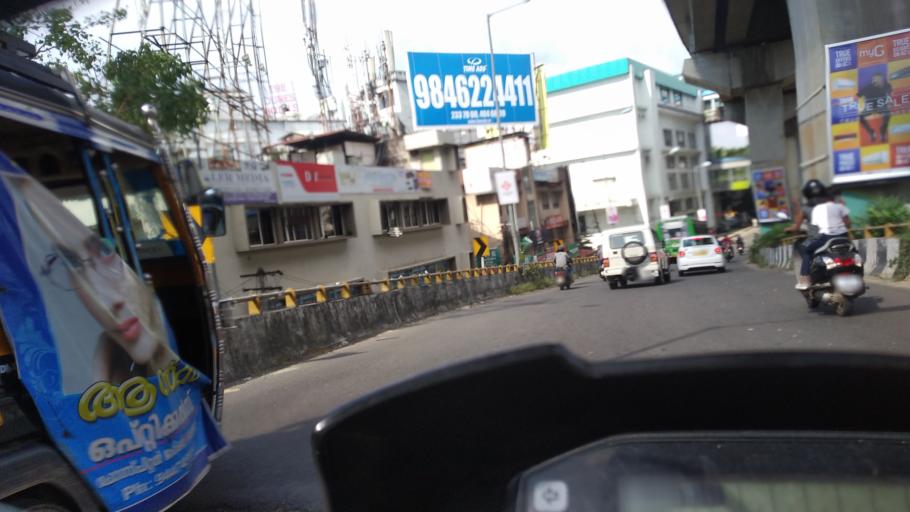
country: IN
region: Kerala
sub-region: Ernakulam
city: Cochin
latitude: 9.9905
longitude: 76.2873
